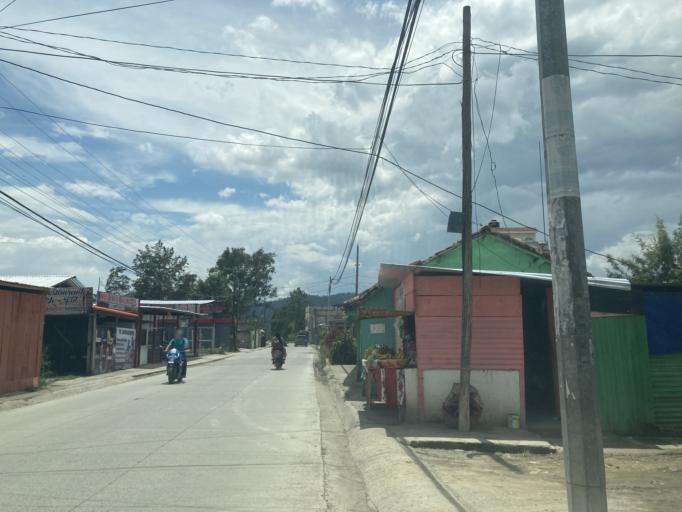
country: GT
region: Huehuetenango
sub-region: Municipio de Huehuetenango
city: Huehuetenango
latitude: 15.3198
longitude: -91.4949
